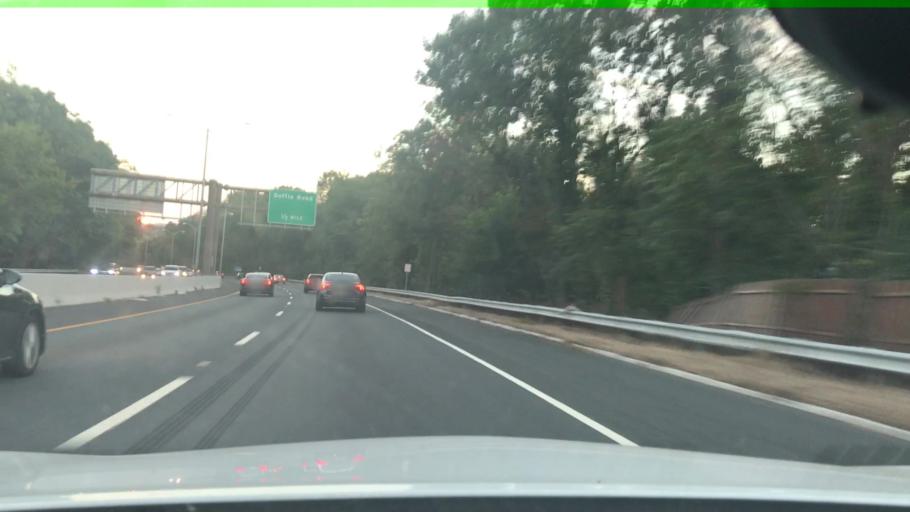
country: US
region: New Jersey
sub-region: Passaic County
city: Hawthorne
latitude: 40.9731
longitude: -74.1597
